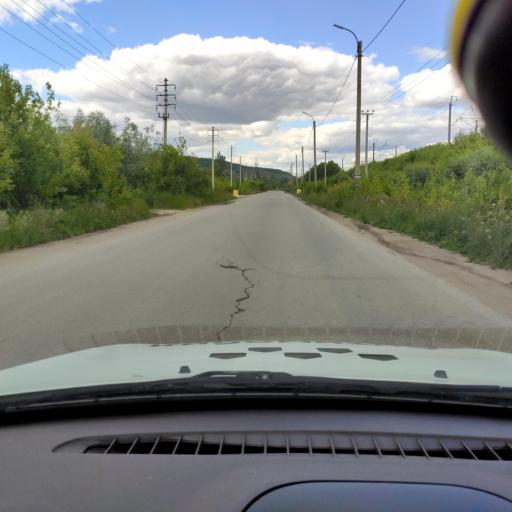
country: RU
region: Samara
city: Zhigulevsk
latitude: 53.4089
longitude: 49.4866
